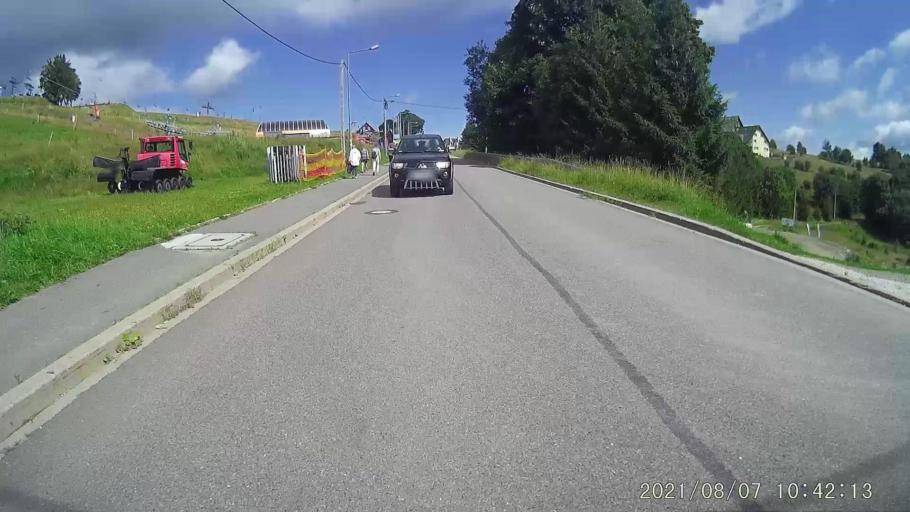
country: PL
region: Lower Silesian Voivodeship
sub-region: Powiat klodzki
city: Duszniki-Zdroj
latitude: 50.3331
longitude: 16.3894
